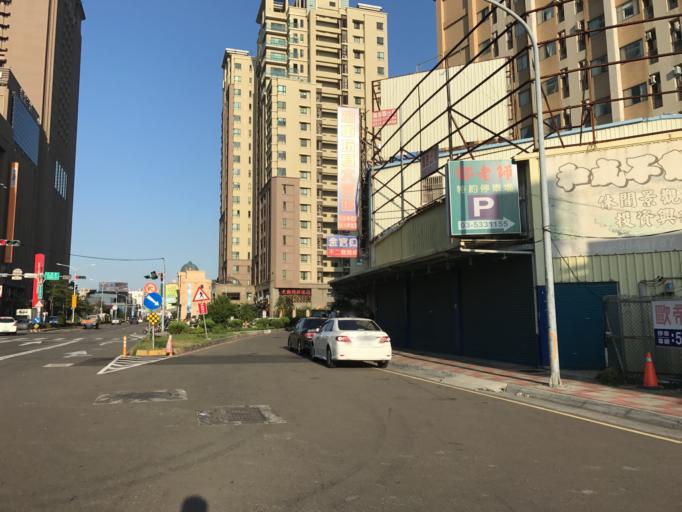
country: TW
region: Taiwan
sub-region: Hsinchu
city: Hsinchu
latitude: 24.8051
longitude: 120.9767
